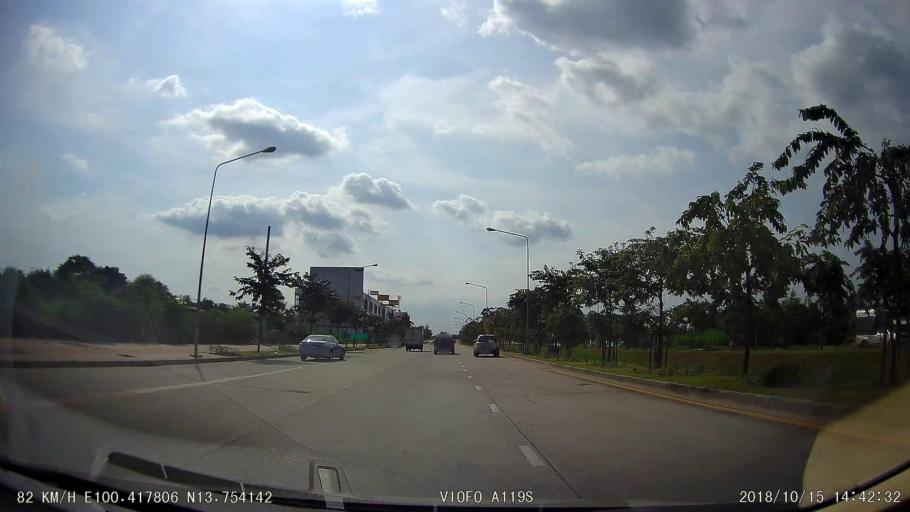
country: TH
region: Bangkok
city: Phasi Charoen
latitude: 13.7541
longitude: 100.4175
